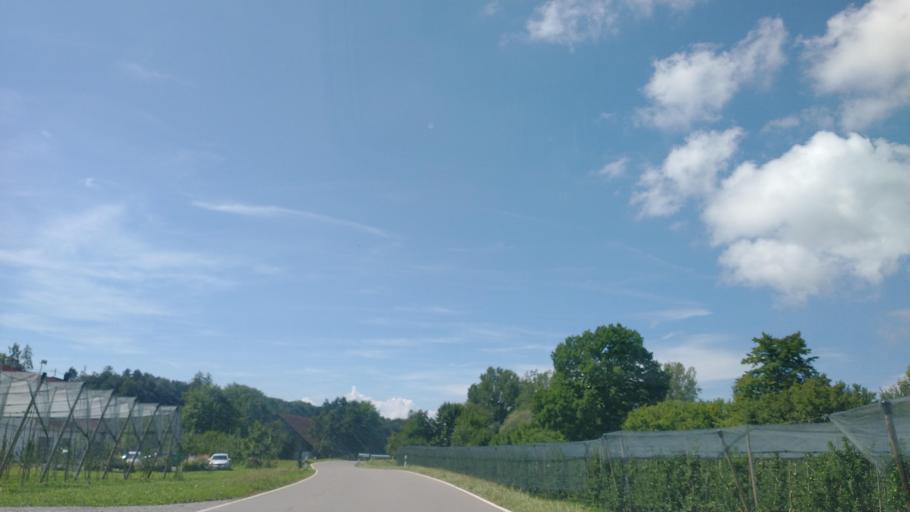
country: DE
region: Baden-Wuerttemberg
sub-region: Tuebingen Region
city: Kressbronn am Bodensee
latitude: 47.6255
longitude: 9.5961
